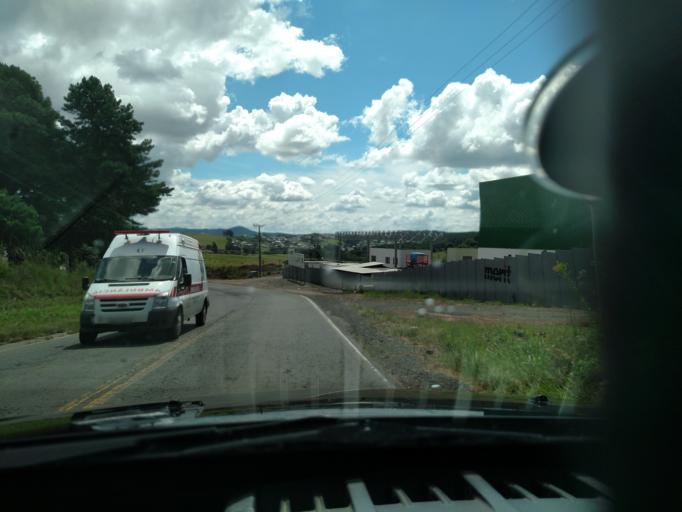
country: BR
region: Santa Catarina
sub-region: Lages
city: Lages
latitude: -27.8168
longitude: -50.2626
